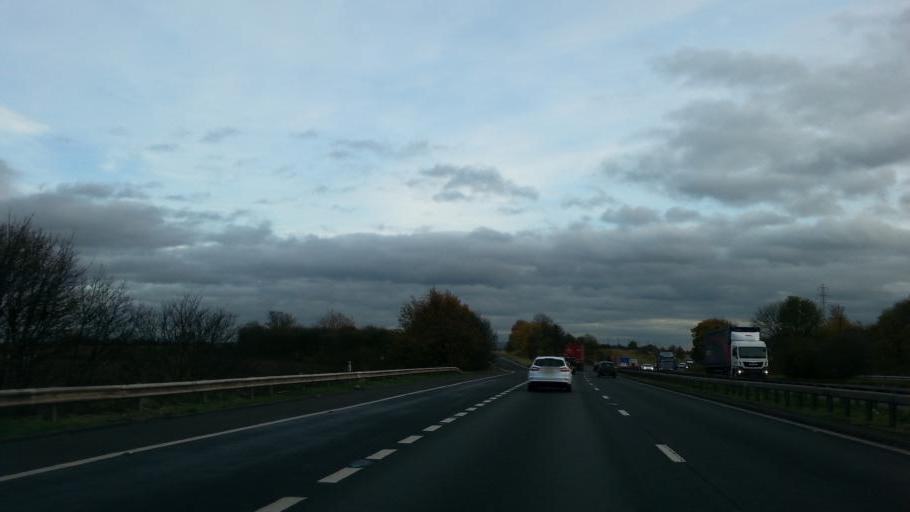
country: GB
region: England
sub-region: Doncaster
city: Bentley
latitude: 53.5216
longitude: -1.1792
